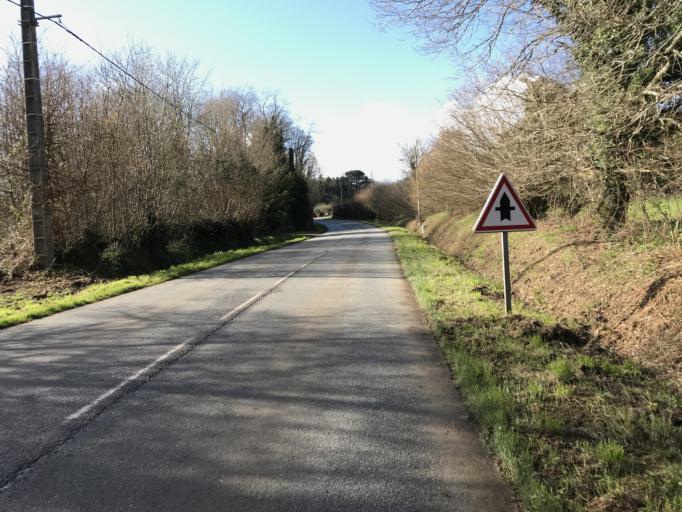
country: FR
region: Brittany
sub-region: Departement du Finistere
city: Loperhet
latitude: 48.3784
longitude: -4.3205
